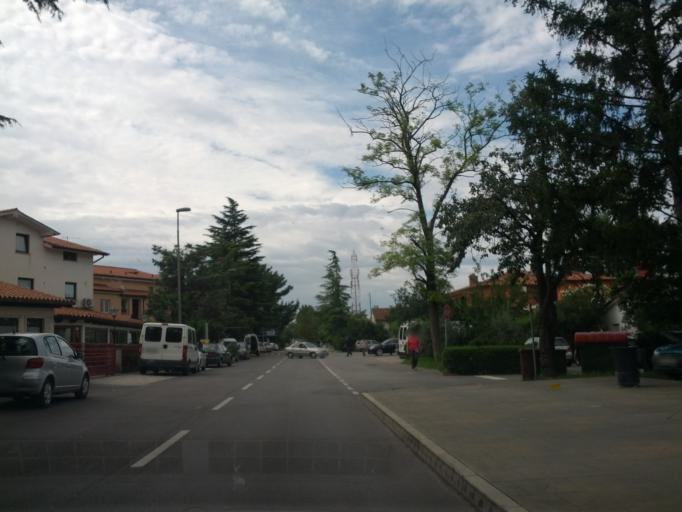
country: SI
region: Koper-Capodistria
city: Koper
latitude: 45.5309
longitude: 13.7378
